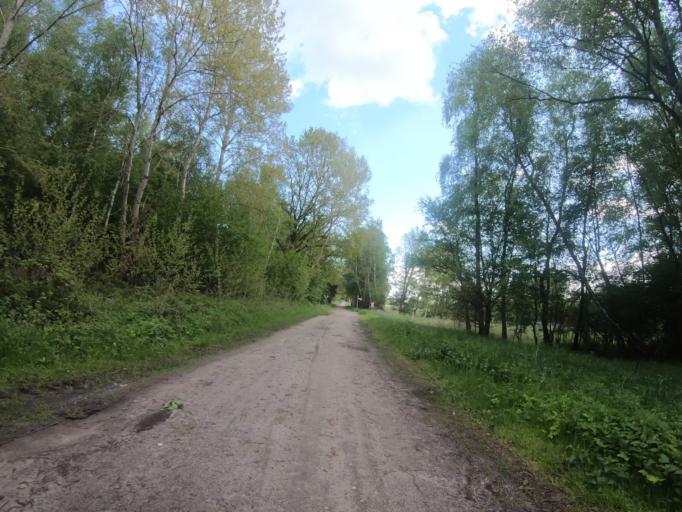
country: DE
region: Lower Saxony
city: Sassenburg
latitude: 52.5188
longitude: 10.6252
